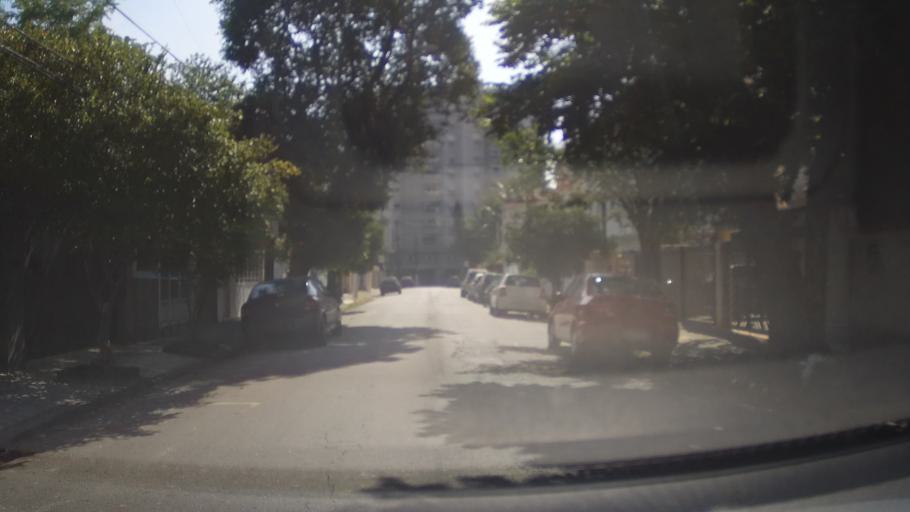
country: BR
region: Sao Paulo
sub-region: Santos
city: Santos
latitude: -23.9883
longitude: -46.3074
